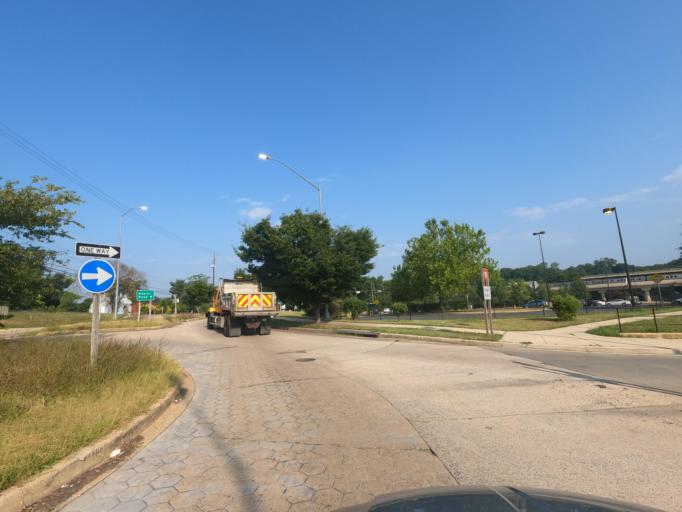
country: US
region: Maryland
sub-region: Prince George's County
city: Silver Hill
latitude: 38.8493
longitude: -76.9565
